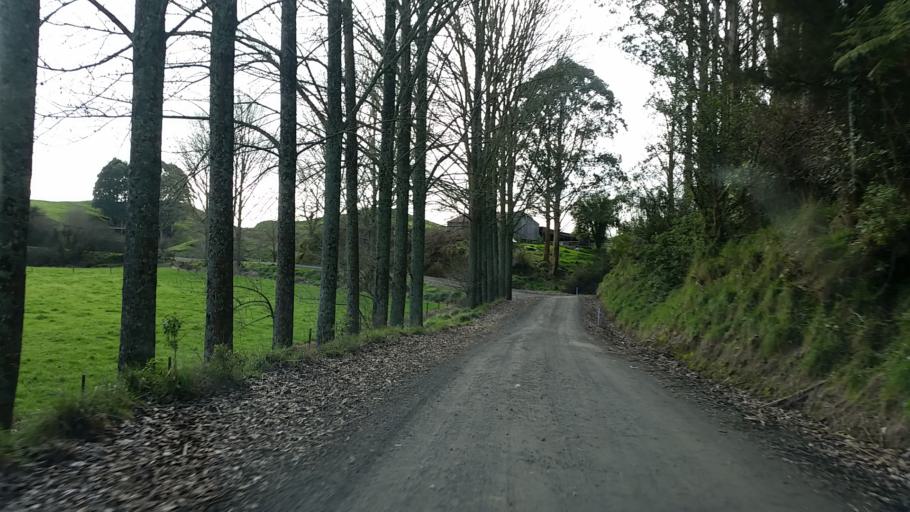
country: NZ
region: Taranaki
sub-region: South Taranaki District
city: Eltham
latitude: -39.2545
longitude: 174.5101
